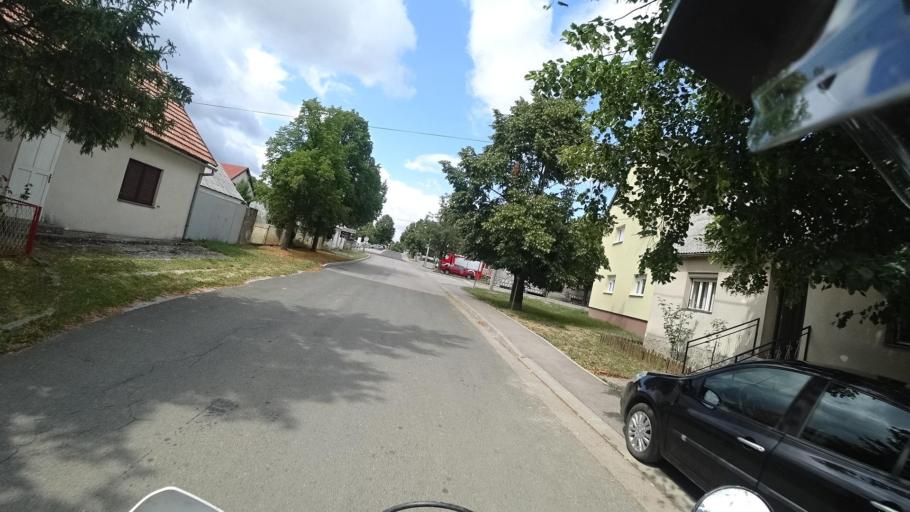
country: HR
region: Zadarska
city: Gracac
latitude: 44.5309
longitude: 15.7669
